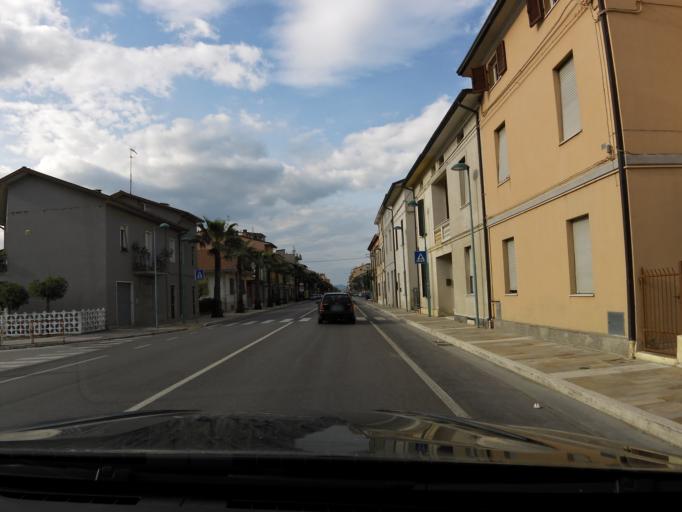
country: IT
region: The Marches
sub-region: Provincia di Macerata
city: Porto Potenza Picena
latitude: 43.3556
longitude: 13.6989
